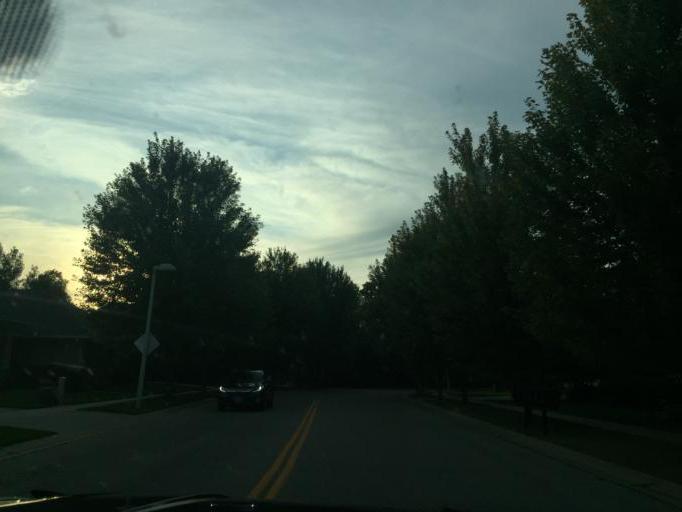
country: US
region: Minnesota
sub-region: Olmsted County
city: Rochester
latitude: 44.0099
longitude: -92.5012
